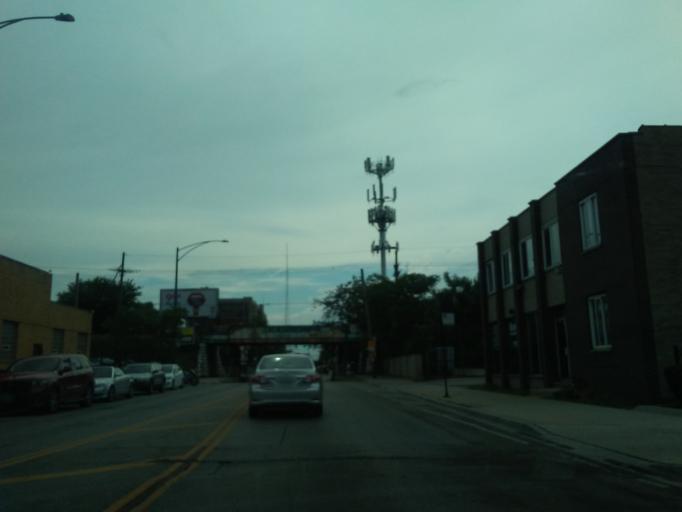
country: US
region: Illinois
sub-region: Cook County
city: Lincolnwood
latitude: 41.9389
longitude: -87.7412
